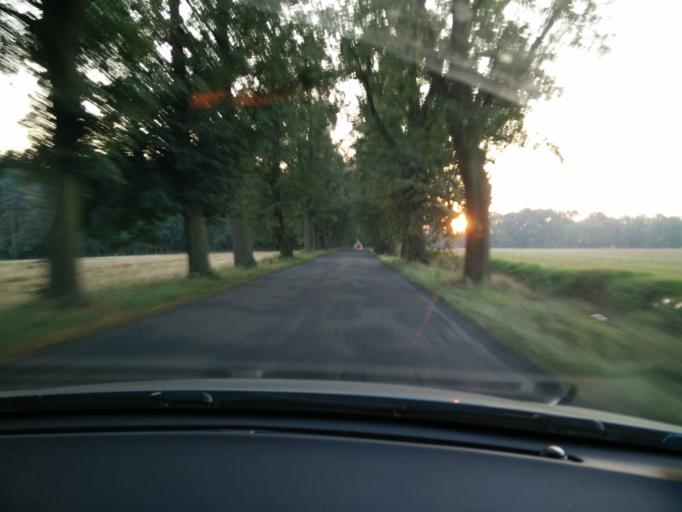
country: PL
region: Greater Poland Voivodeship
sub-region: Powiat wrzesinski
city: Miloslaw
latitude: 52.2048
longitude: 17.4587
